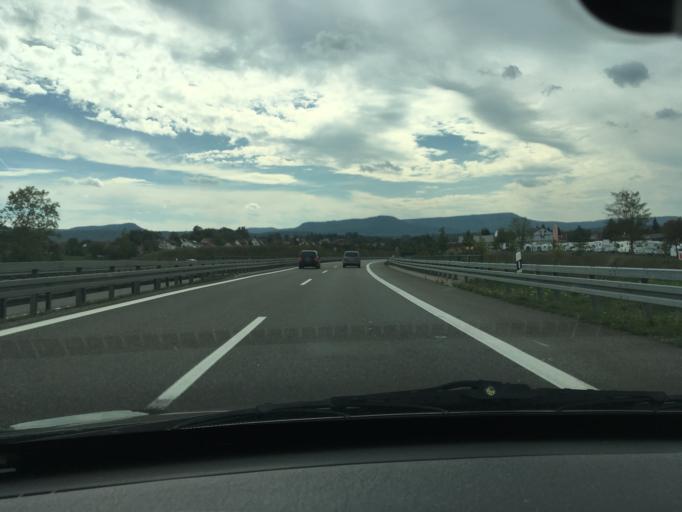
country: DE
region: Baden-Wuerttemberg
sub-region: Tuebingen Region
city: Dusslingen
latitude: 48.4578
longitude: 9.0621
